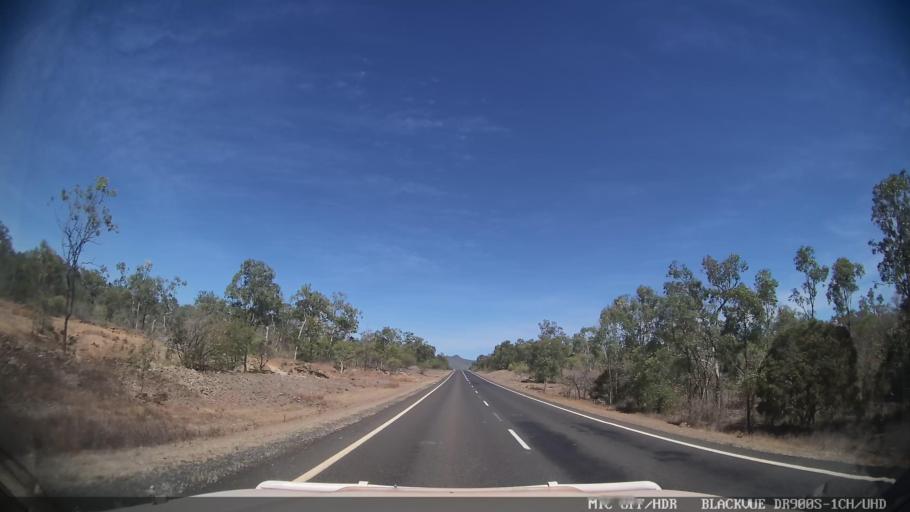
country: AU
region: Queensland
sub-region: Cook
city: Cooktown
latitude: -15.7022
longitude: 144.6071
